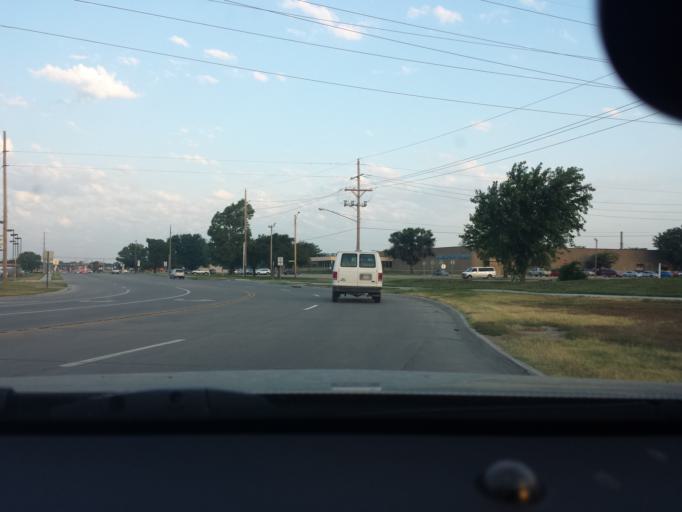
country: US
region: Kansas
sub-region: Riley County
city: Manhattan
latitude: 39.1895
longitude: -96.5448
